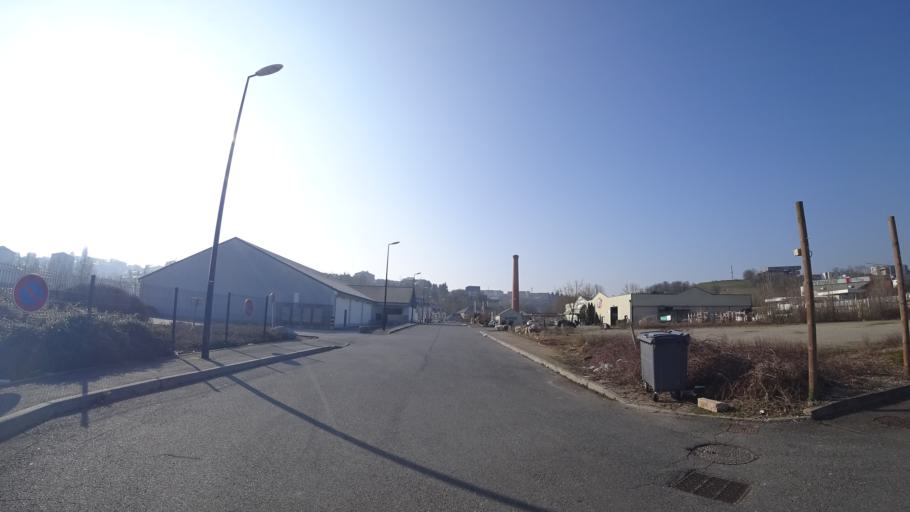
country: FR
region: Midi-Pyrenees
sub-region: Departement de l'Aveyron
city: Rodez
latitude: 44.3629
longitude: 2.5679
